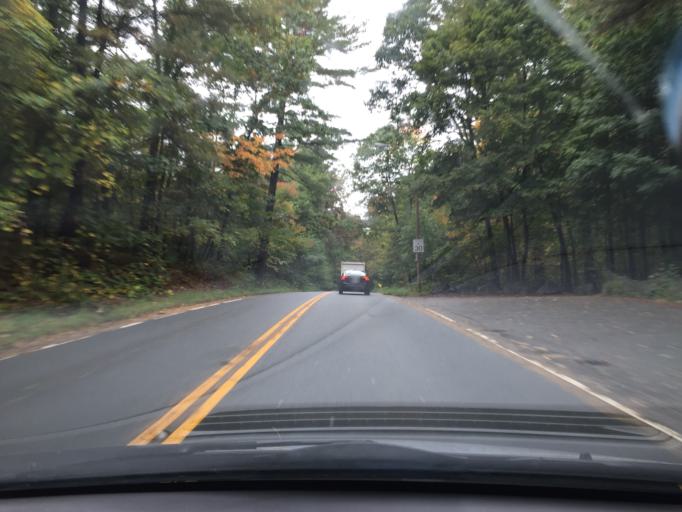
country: US
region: Massachusetts
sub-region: Middlesex County
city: Winchester
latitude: 42.4464
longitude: -71.1251
